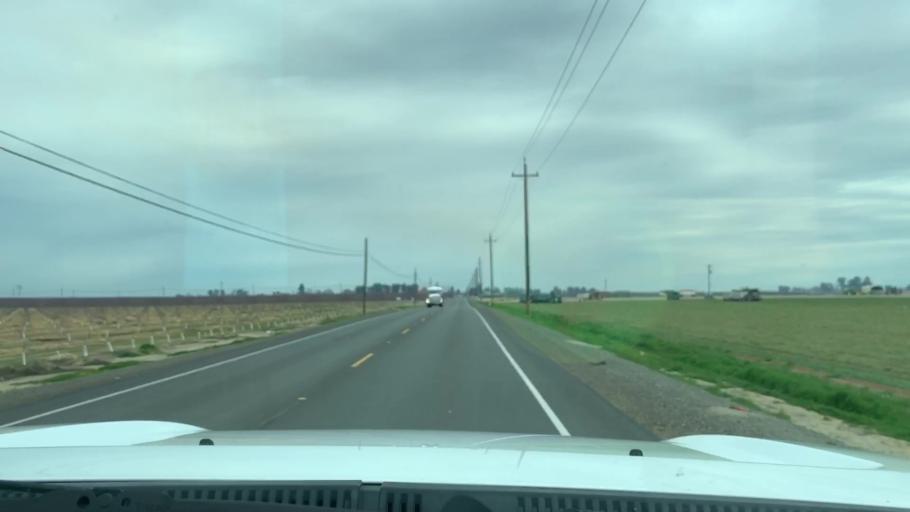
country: US
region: California
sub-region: Kern County
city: Shafter
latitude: 35.4095
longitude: -119.2519
